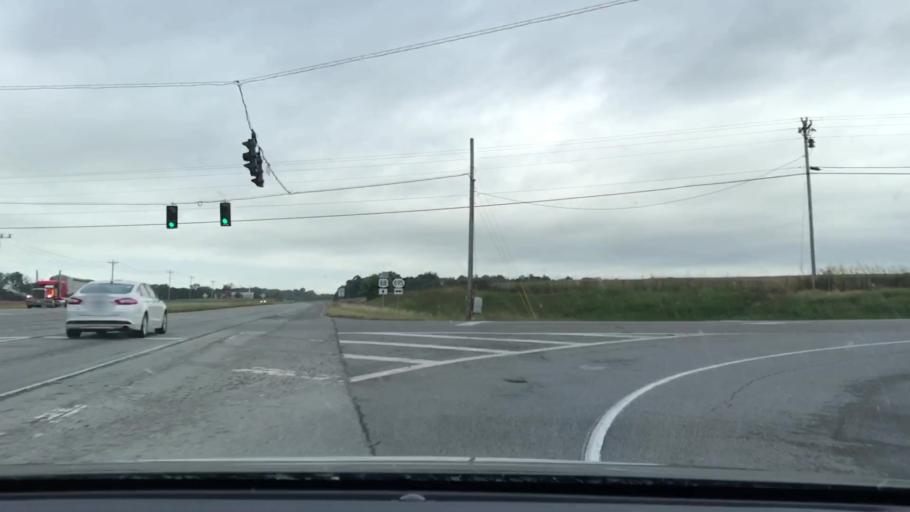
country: US
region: Kentucky
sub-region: Christian County
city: Hopkinsville
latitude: 36.8341
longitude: -87.5290
